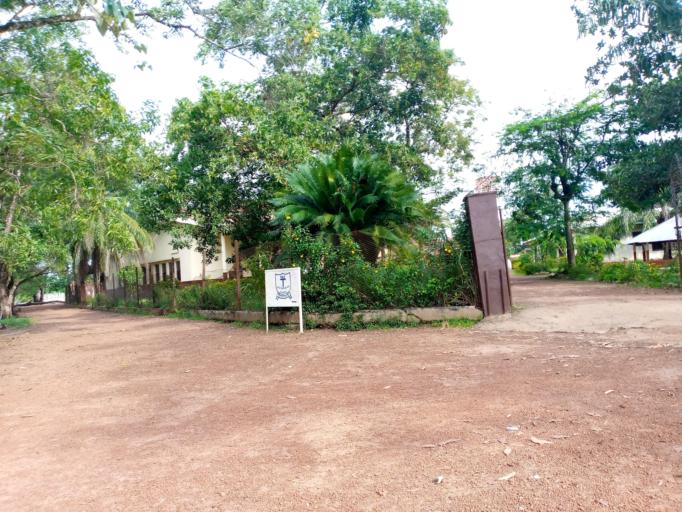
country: SL
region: Northern Province
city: Magburaka
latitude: 8.7163
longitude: -11.9507
